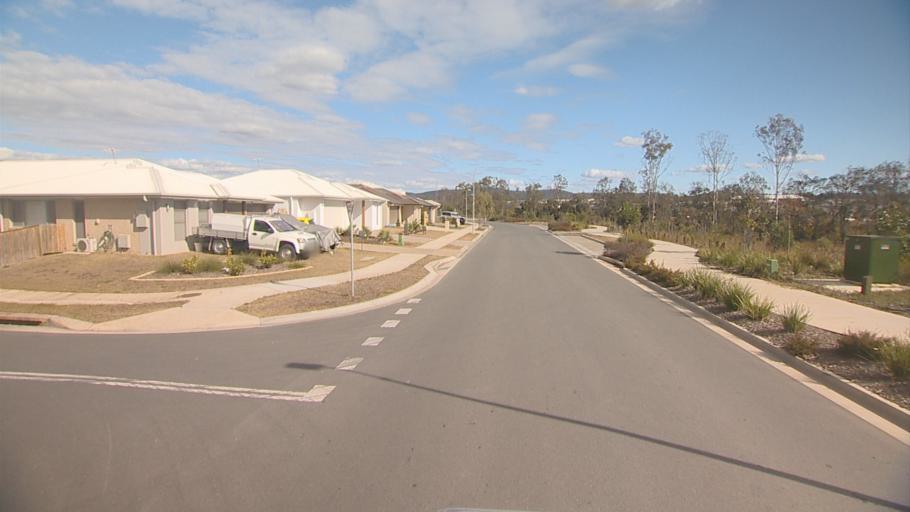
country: AU
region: Queensland
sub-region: Logan
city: Chambers Flat
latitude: -27.7993
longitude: 153.1138
